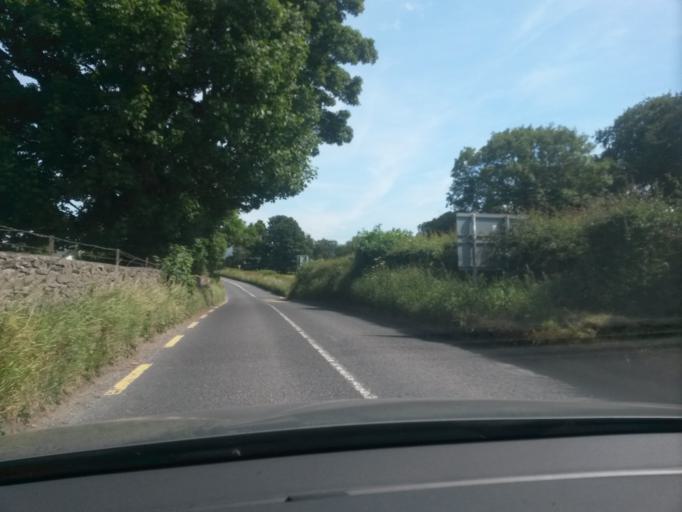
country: IE
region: Leinster
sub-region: Wicklow
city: Blessington
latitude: 53.1747
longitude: -6.5561
